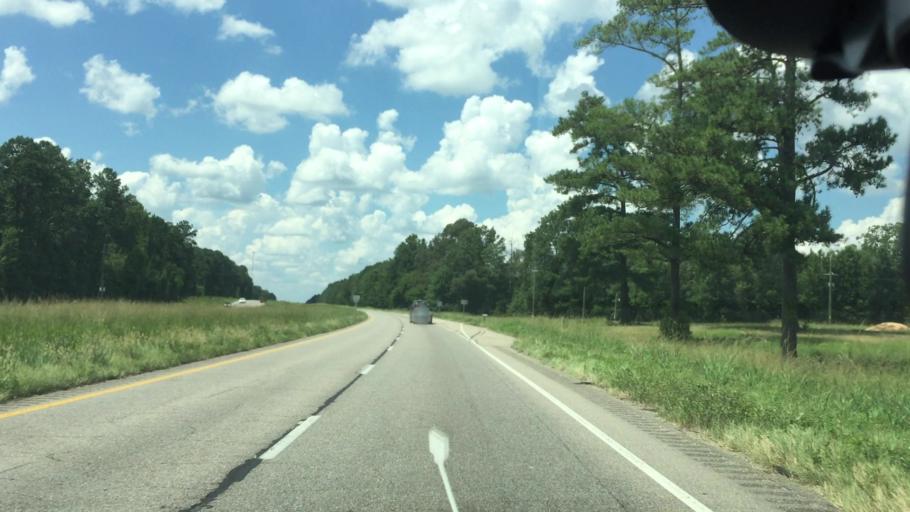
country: US
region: Alabama
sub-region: Montgomery County
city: Pike Road
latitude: 32.1175
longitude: -86.0691
